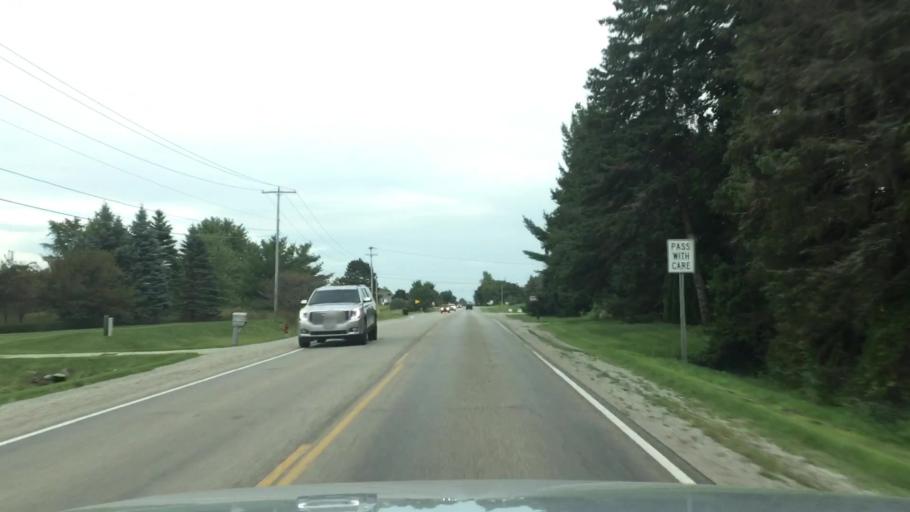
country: US
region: Michigan
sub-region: Genesee County
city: Grand Blanc
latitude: 42.8862
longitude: -83.6601
